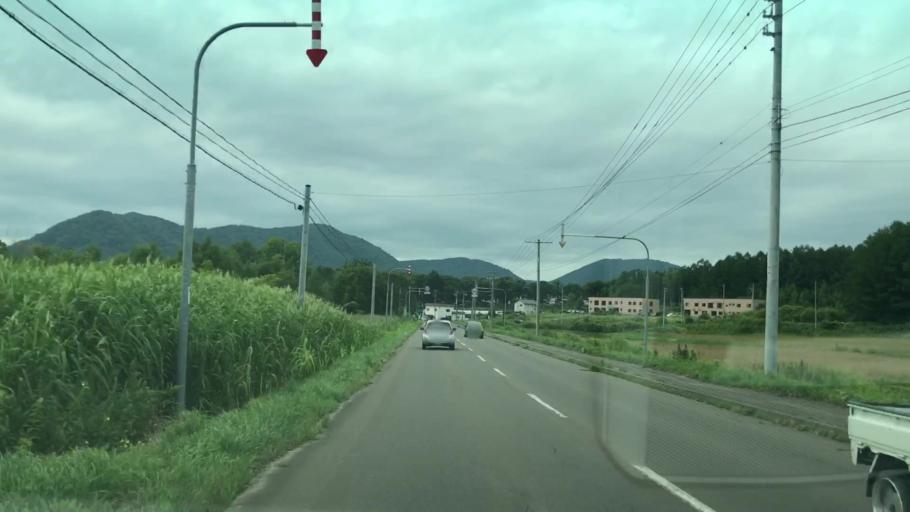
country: JP
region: Hokkaido
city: Yoichi
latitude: 43.0910
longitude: 140.8173
